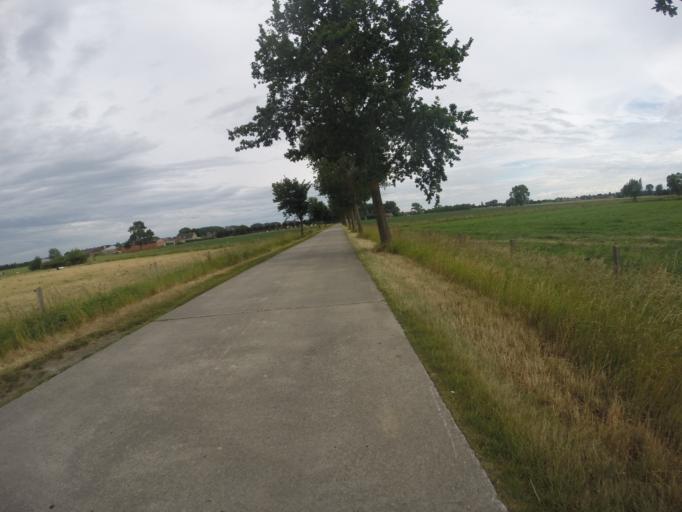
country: BE
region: Flanders
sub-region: Provincie West-Vlaanderen
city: Ruiselede
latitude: 51.0259
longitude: 3.3714
